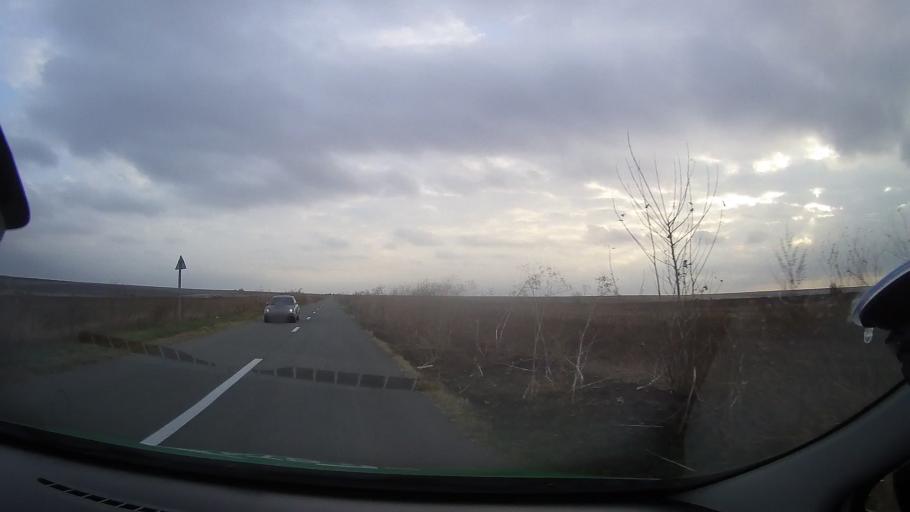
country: RO
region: Constanta
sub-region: Comuna Pestera
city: Pestera
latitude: 44.1503
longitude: 28.1140
